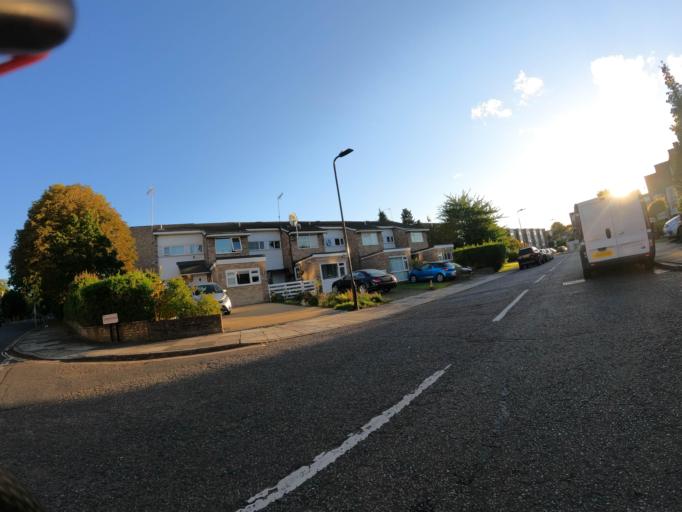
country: GB
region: England
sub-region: Greater London
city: Ealing Broadway
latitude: 51.5242
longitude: -0.3179
